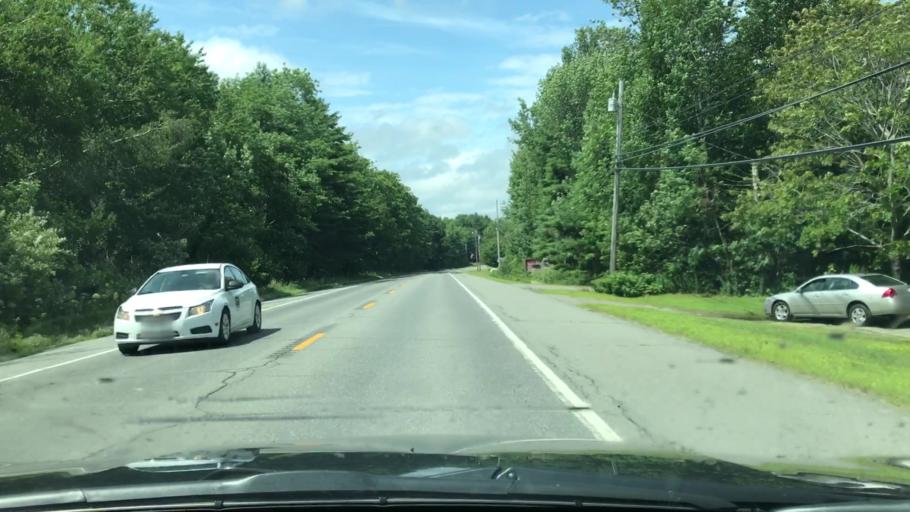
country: US
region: Maine
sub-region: Waldo County
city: Northport
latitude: 44.3698
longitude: -68.9819
